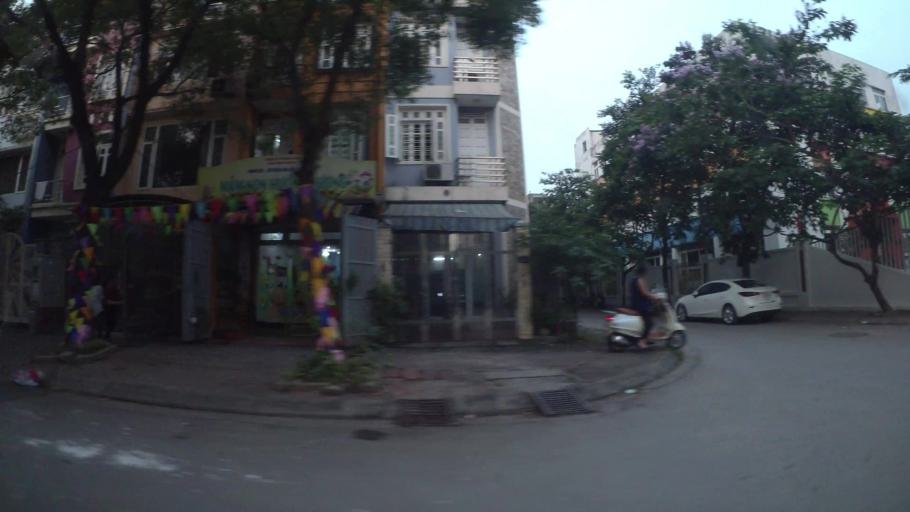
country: VN
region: Ha Noi
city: Thanh Xuan
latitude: 20.9791
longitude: 105.7950
